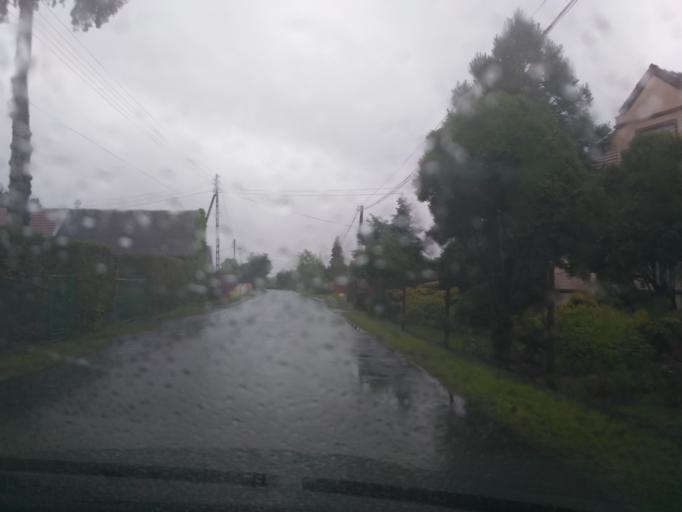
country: PL
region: Subcarpathian Voivodeship
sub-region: Powiat jasielski
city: Jaslo
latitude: 49.7413
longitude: 21.5011
